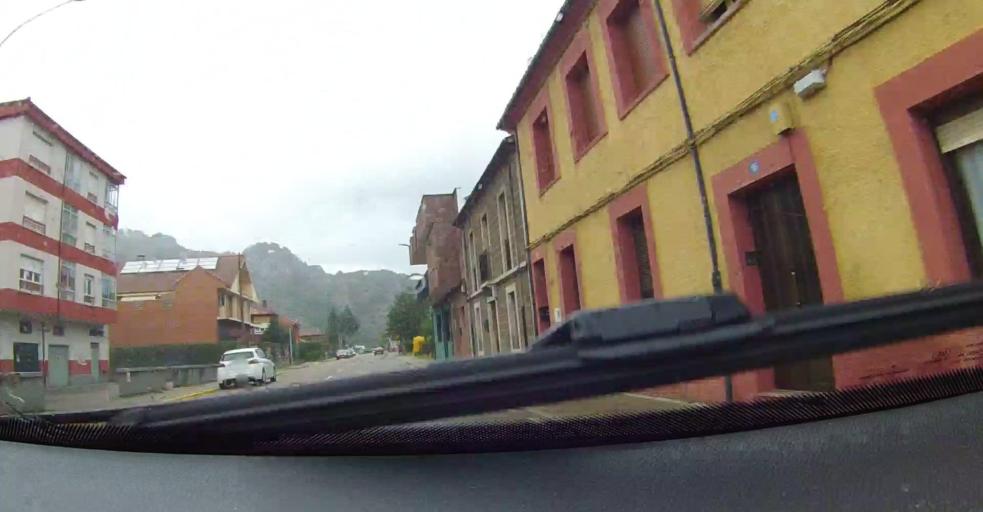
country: ES
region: Castille and Leon
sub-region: Provincia de Leon
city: Cistierna
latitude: 42.8071
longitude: -5.1297
